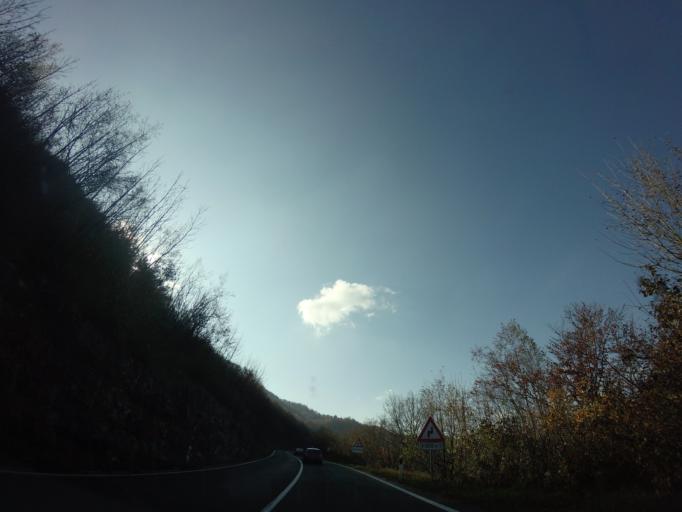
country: HR
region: Licko-Senjska
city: Jezerce
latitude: 44.9289
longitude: 15.6251
